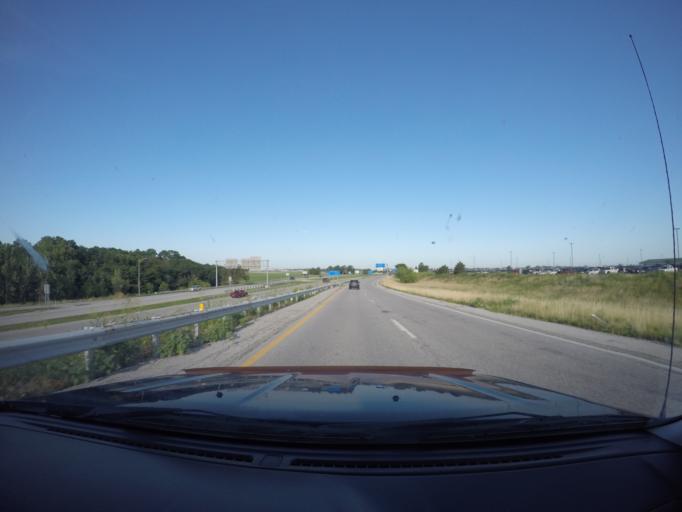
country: US
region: Missouri
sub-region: Platte County
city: Weatherby Lake
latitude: 39.3115
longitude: -94.6908
